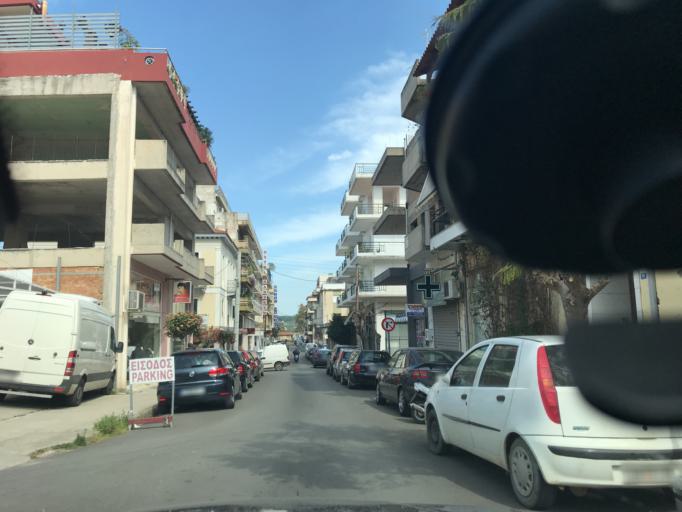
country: GR
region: West Greece
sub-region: Nomos Ileias
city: Pyrgos
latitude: 37.6743
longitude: 21.4372
